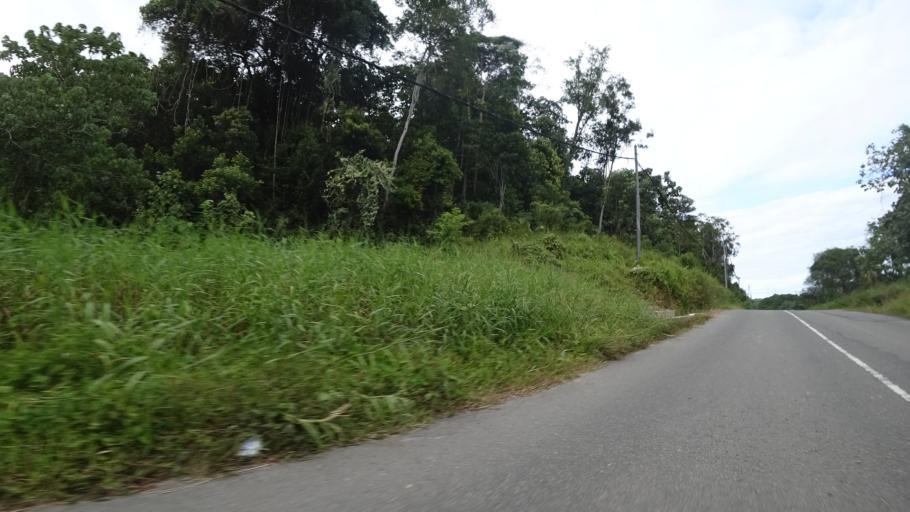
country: BN
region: Brunei and Muara
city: Bandar Seri Begawan
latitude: 4.8494
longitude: 114.9537
